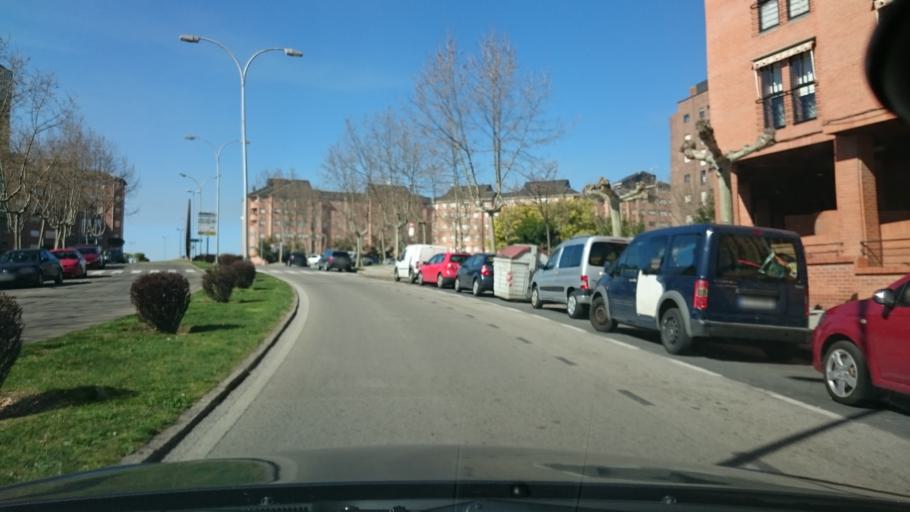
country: ES
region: Castille and Leon
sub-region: Provincia de Leon
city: Ponferrada
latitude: 42.5547
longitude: -6.5941
